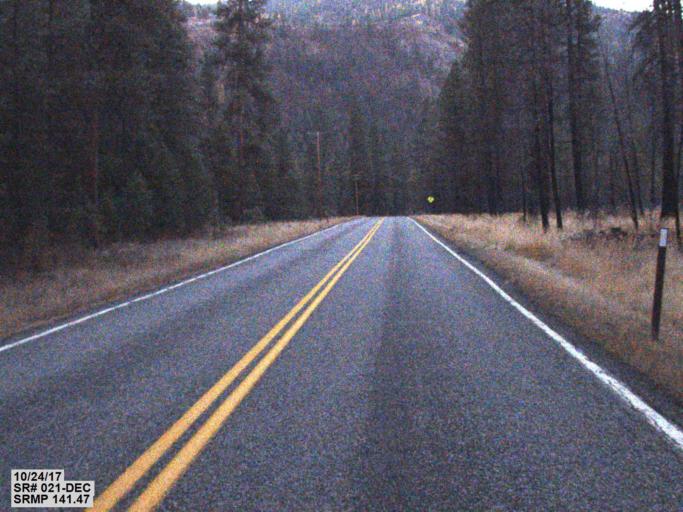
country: US
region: Washington
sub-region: Ferry County
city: Republic
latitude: 48.4052
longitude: -118.7334
